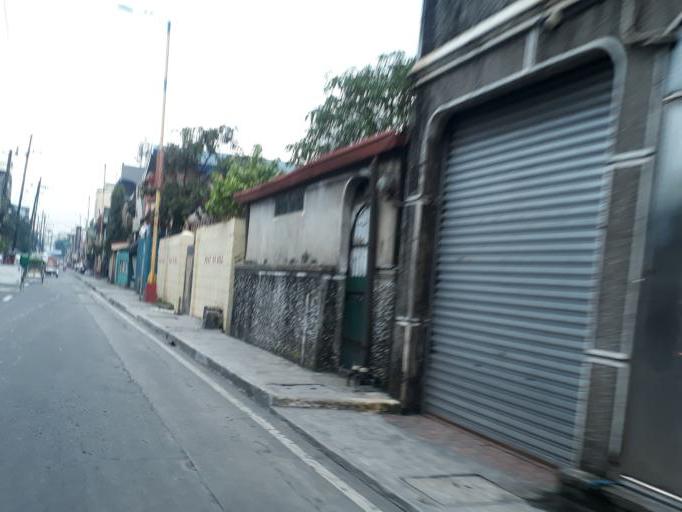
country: PH
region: Metro Manila
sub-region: Caloocan City
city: Niugan
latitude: 14.6533
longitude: 120.9495
